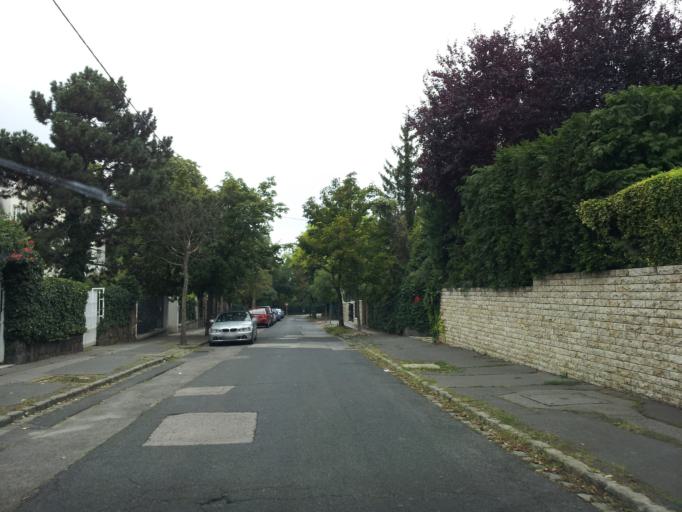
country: HU
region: Budapest
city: Budapest II. keruelet
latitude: 47.5228
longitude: 19.0258
